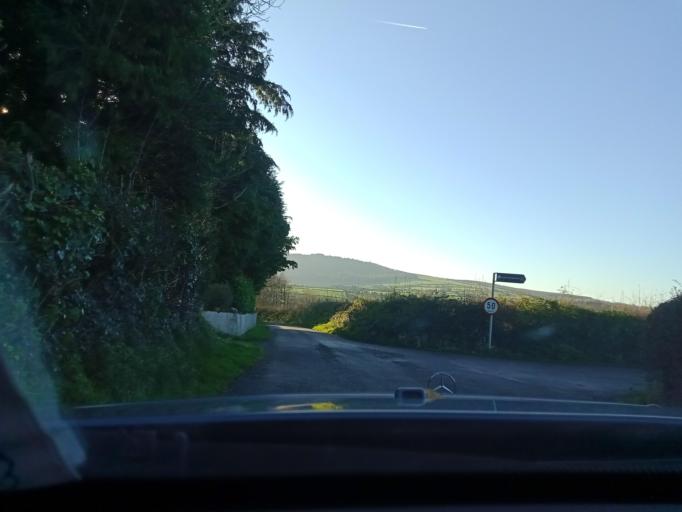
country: IE
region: Munster
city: Carrick-on-Suir
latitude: 52.4333
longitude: -7.3934
